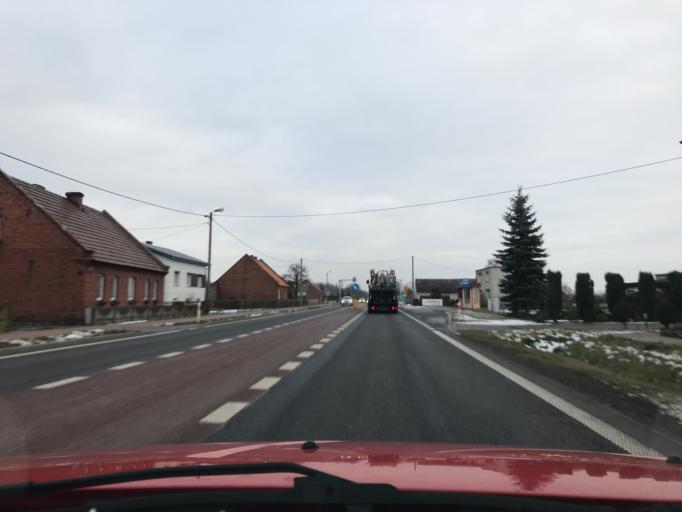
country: PL
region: Greater Poland Voivodeship
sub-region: Powiat pleszewski
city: Goluchow
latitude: 51.8661
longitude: 17.9009
